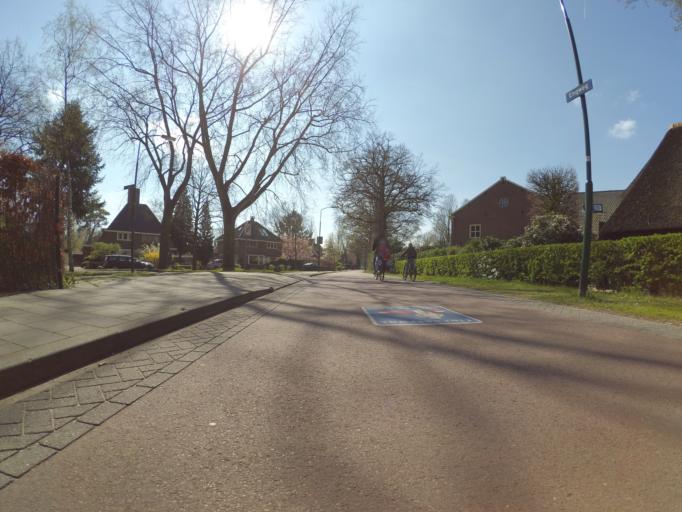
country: NL
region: Utrecht
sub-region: Gemeente Utrechtse Heuvelrug
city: Driebergen-Rijsenburg
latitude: 52.0455
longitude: 5.2825
